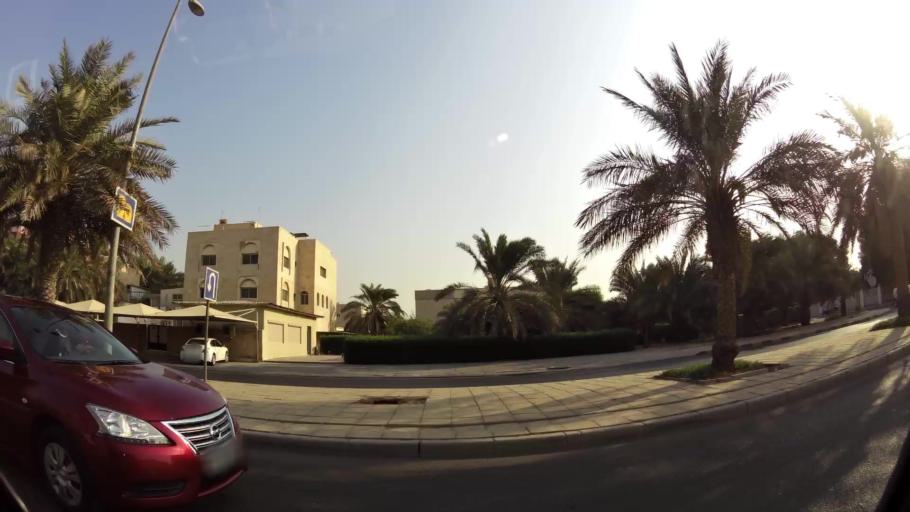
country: KW
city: Bayan
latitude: 29.3027
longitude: 48.0548
